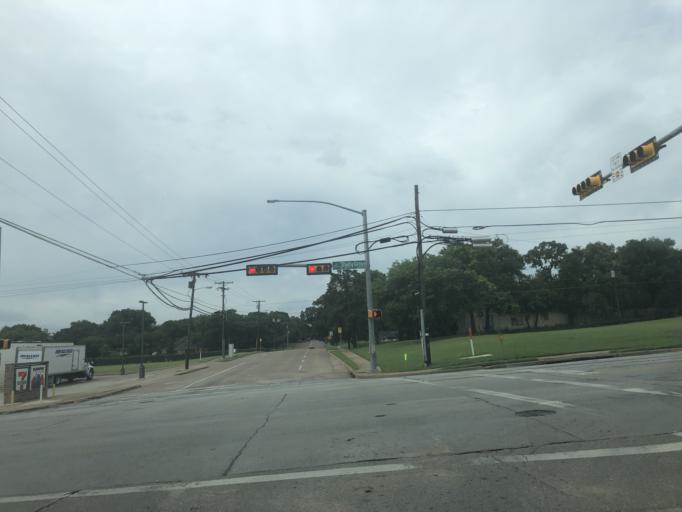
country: US
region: Texas
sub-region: Dallas County
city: Irving
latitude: 32.8014
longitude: -96.9469
